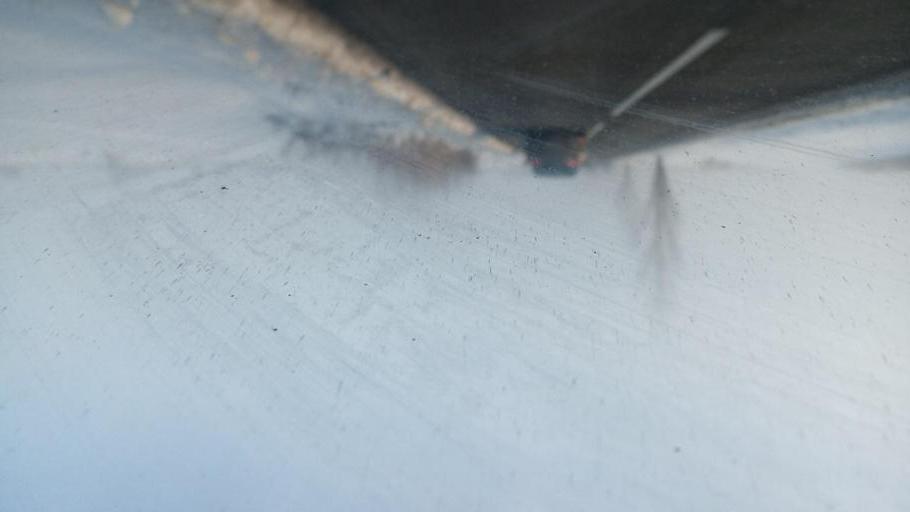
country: RO
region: Suceava
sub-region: Comuna Berchisesti
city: Berchisesti
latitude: 47.5083
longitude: 26.0452
